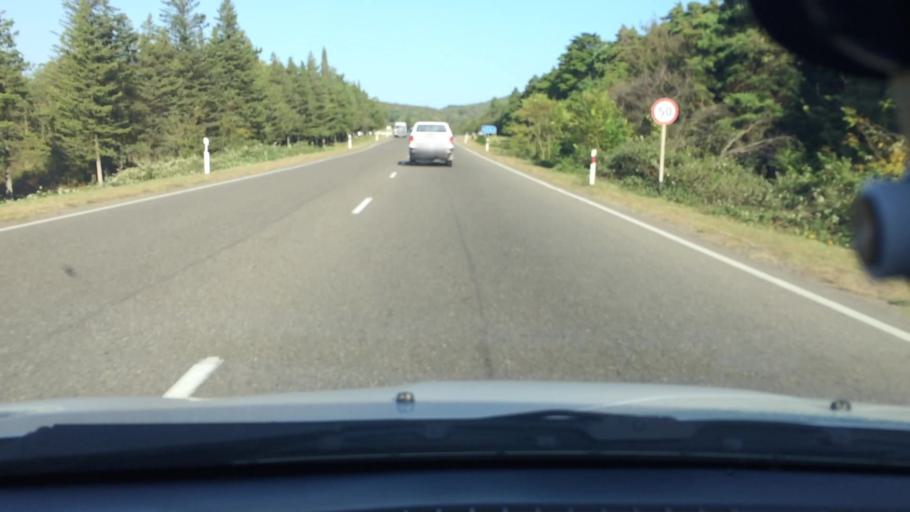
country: GE
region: Imereti
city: Kutaisi
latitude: 42.2372
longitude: 42.7694
